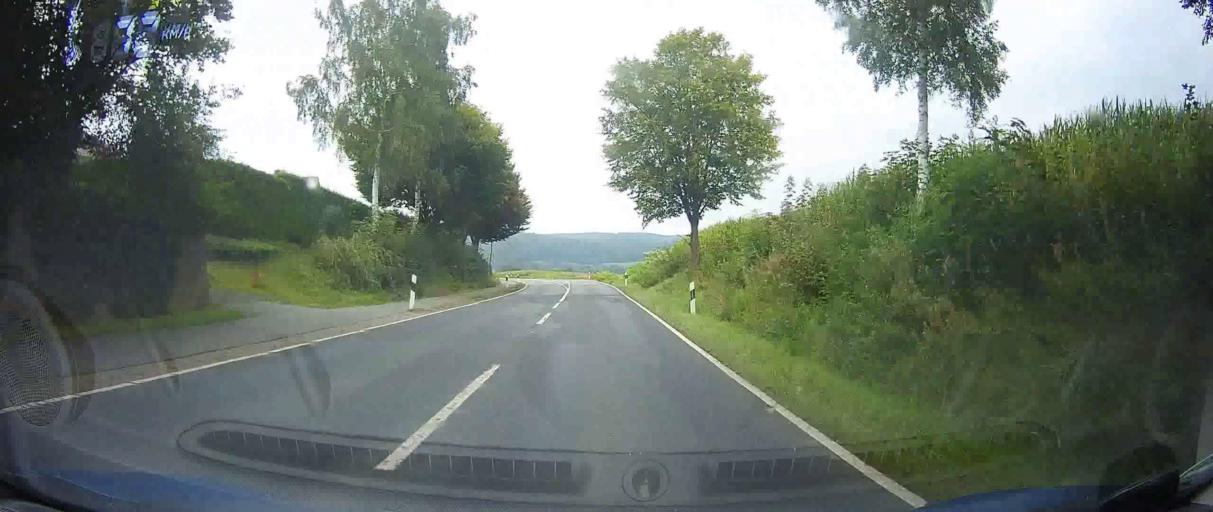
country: DE
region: Lower Saxony
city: Uslar
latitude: 51.6691
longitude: 9.6365
